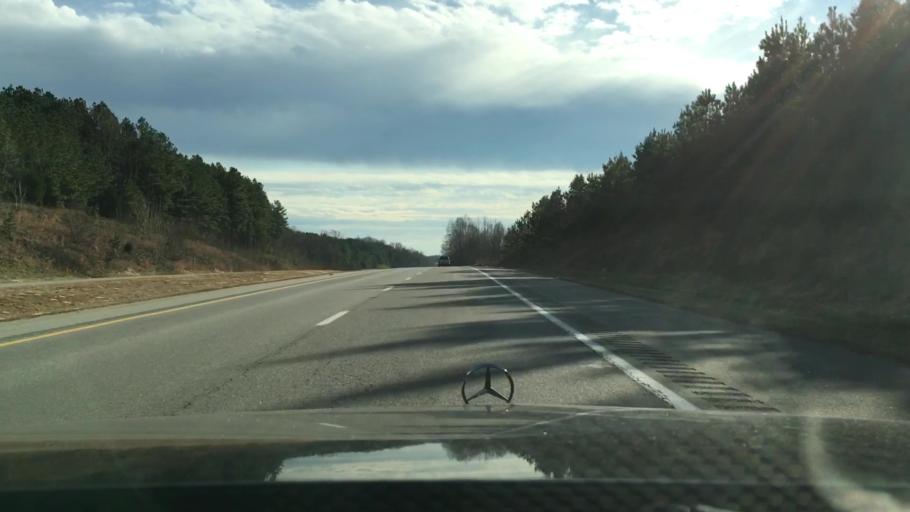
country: US
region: Virginia
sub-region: City of Danville
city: Danville
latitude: 36.6396
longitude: -79.3648
